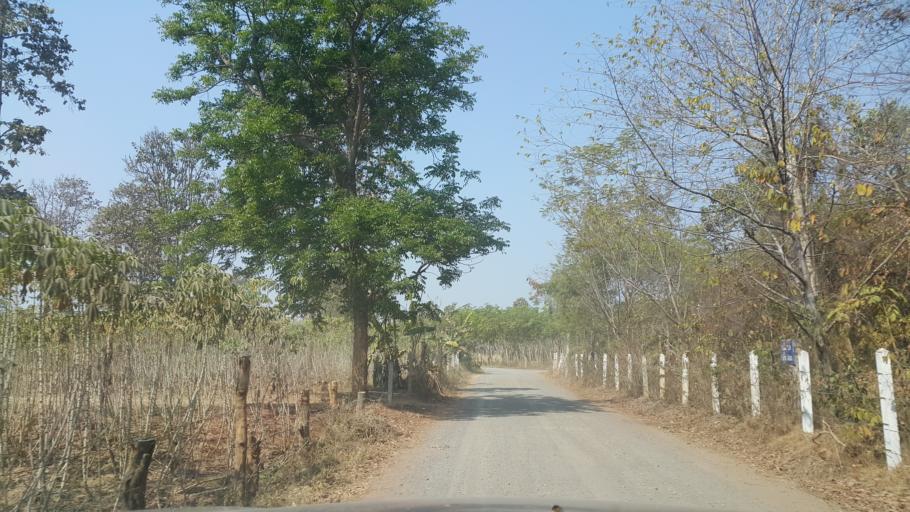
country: TH
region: Buriram
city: Krasang
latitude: 15.0926
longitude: 103.3714
